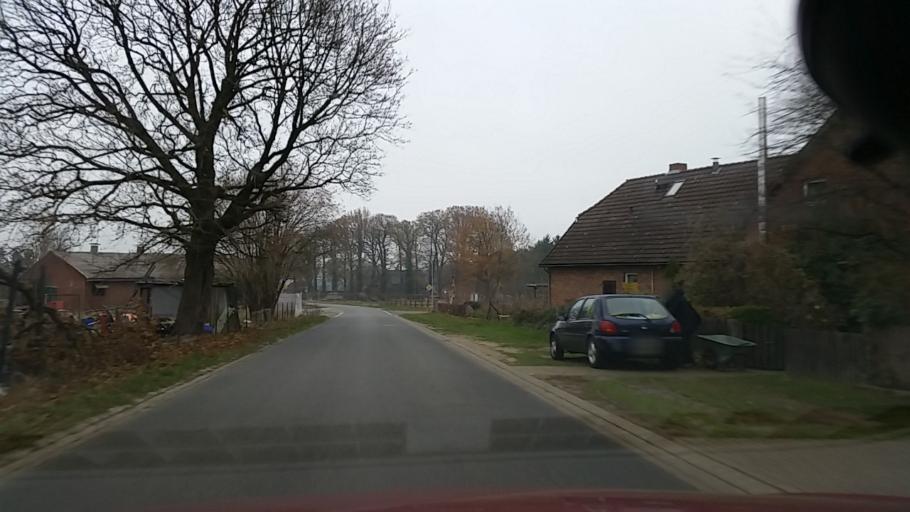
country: DE
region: Lower Saxony
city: Stadensen
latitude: 52.8469
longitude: 10.5625
